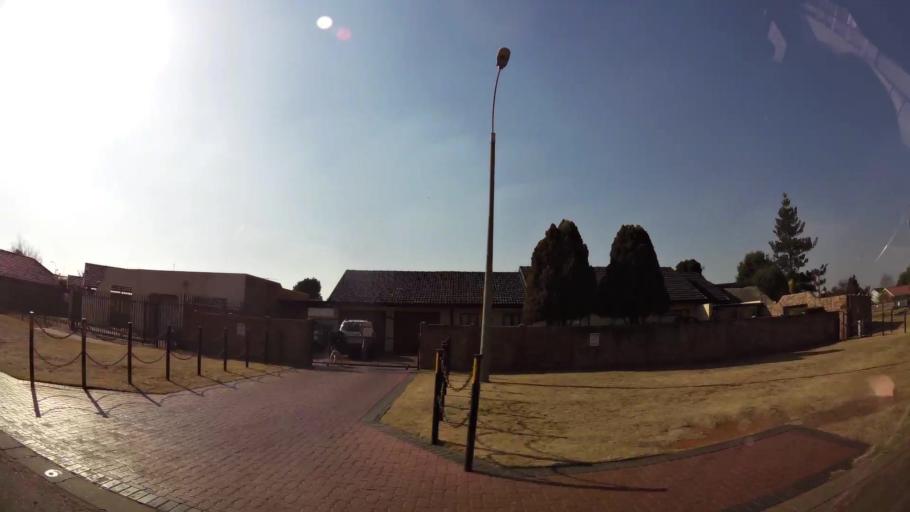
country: ZA
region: Gauteng
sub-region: West Rand District Municipality
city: Randfontein
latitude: -26.1805
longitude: 27.6874
